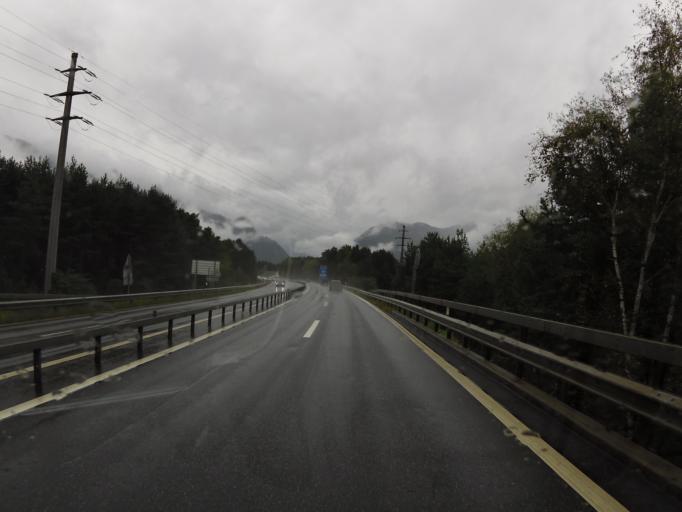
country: CH
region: Grisons
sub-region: Hinterrhein District
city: Thusis
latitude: 46.7096
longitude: 9.4487
